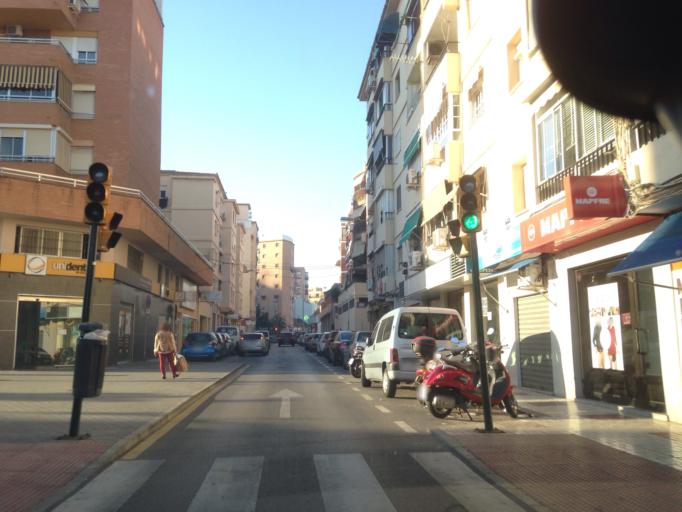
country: ES
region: Andalusia
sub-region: Provincia de Malaga
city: Malaga
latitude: 36.7112
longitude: -4.4388
